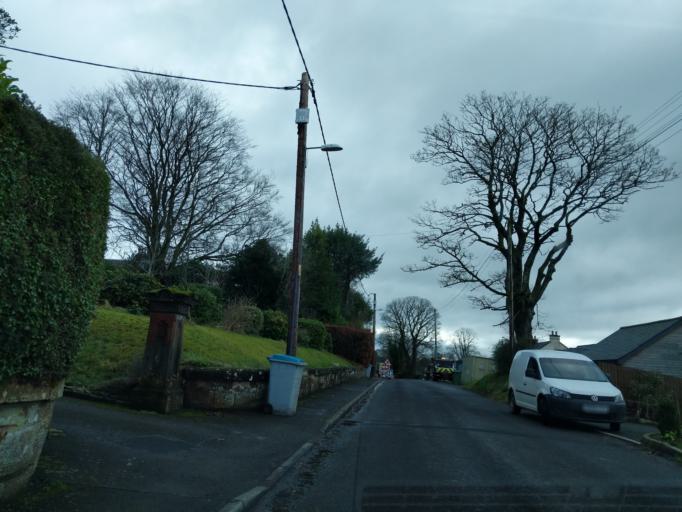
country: GB
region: Scotland
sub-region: Dumfries and Galloway
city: Moffat
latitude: 55.3286
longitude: -3.4322
